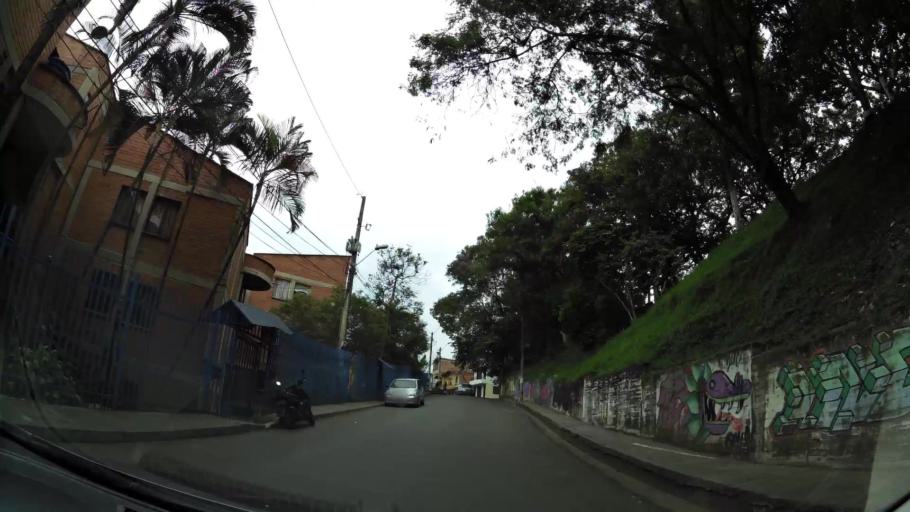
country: CO
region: Antioquia
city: Medellin
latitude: 6.2747
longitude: -75.5602
